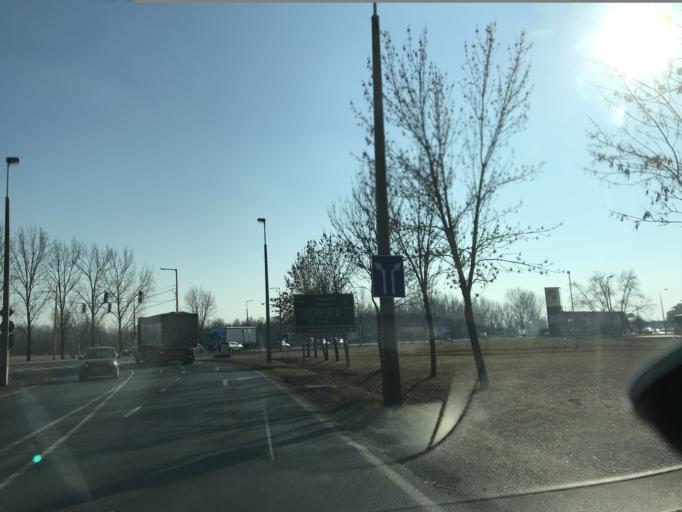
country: HU
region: Gyor-Moson-Sopron
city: Gyor
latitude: 47.6614
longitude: 17.6375
